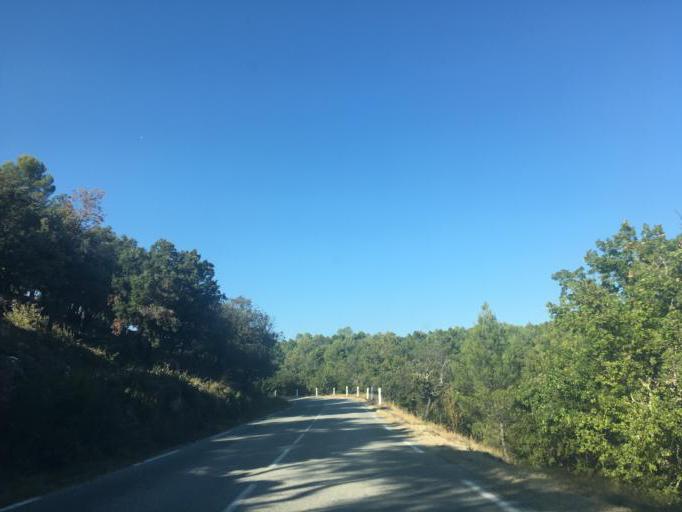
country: FR
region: Provence-Alpes-Cote d'Azur
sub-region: Departement du Var
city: Salernes
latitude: 43.5908
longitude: 6.2245
